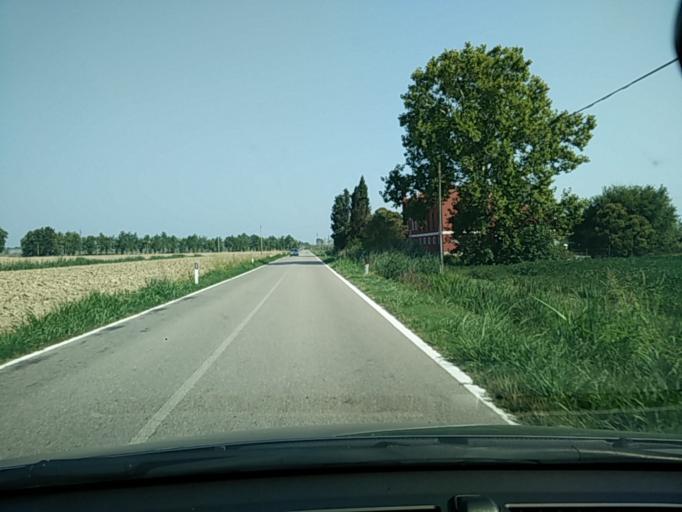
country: IT
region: Veneto
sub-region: Provincia di Venezia
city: Caorle
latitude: 45.6238
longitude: 12.8433
